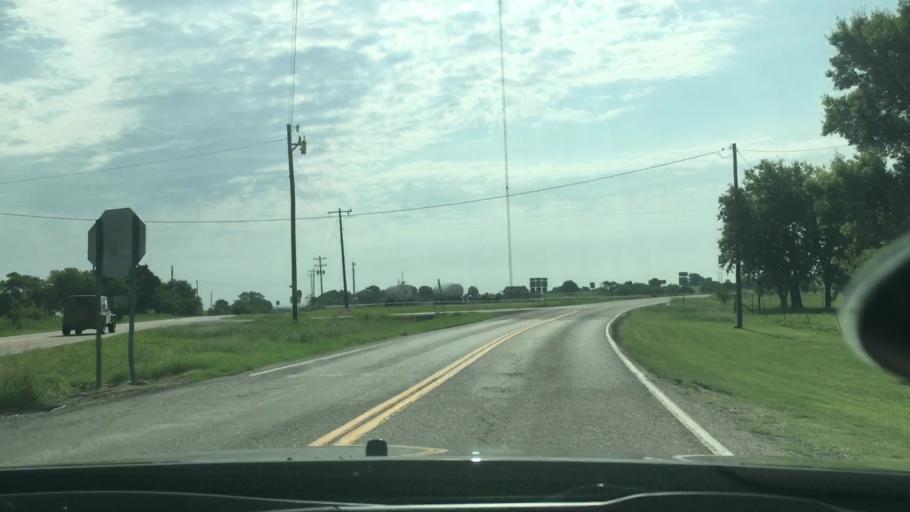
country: US
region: Oklahoma
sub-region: Bryan County
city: Durant
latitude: 34.1432
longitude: -96.4994
